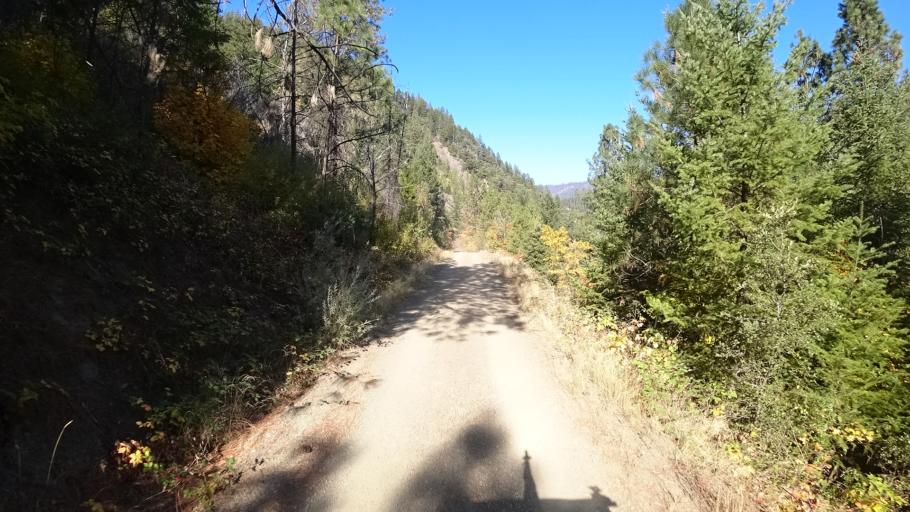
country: US
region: California
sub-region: Siskiyou County
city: Happy Camp
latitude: 41.7668
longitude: -123.0258
